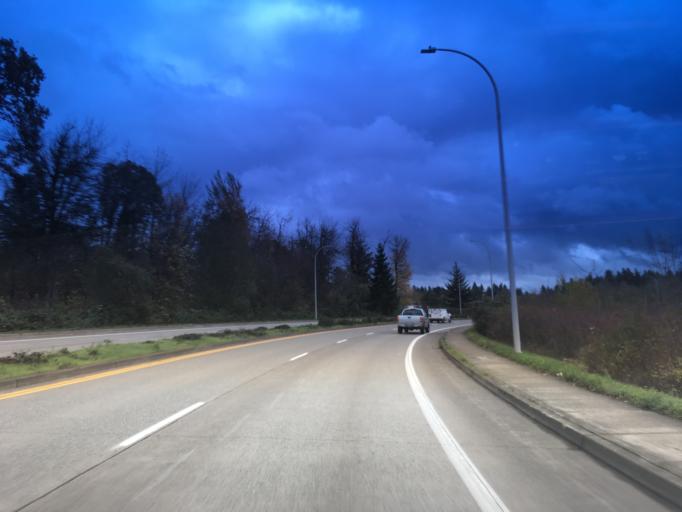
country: US
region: Oregon
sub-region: Multnomah County
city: Fairview
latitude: 45.5312
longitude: -122.4435
